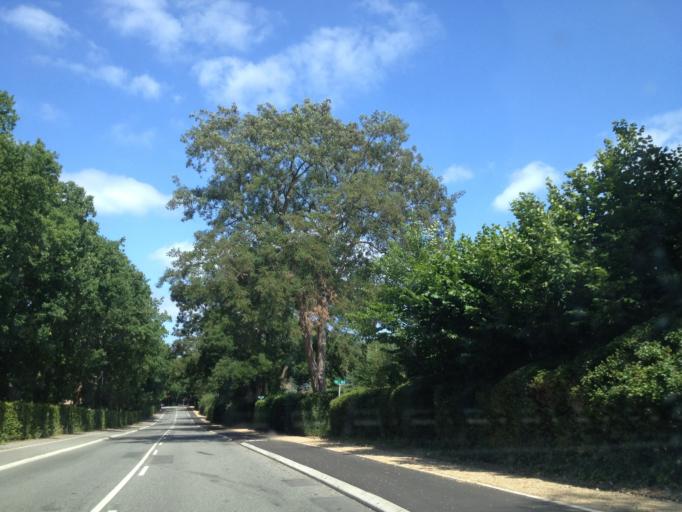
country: DK
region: Capital Region
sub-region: Rudersdal Kommune
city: Trorod
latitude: 55.8235
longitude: 12.5408
